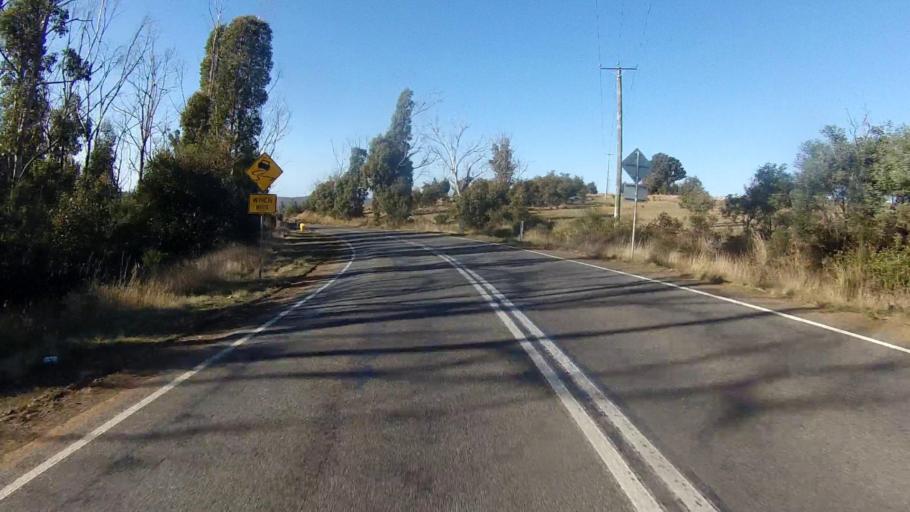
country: AU
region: Tasmania
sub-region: Sorell
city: Sorell
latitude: -42.8442
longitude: 147.8117
